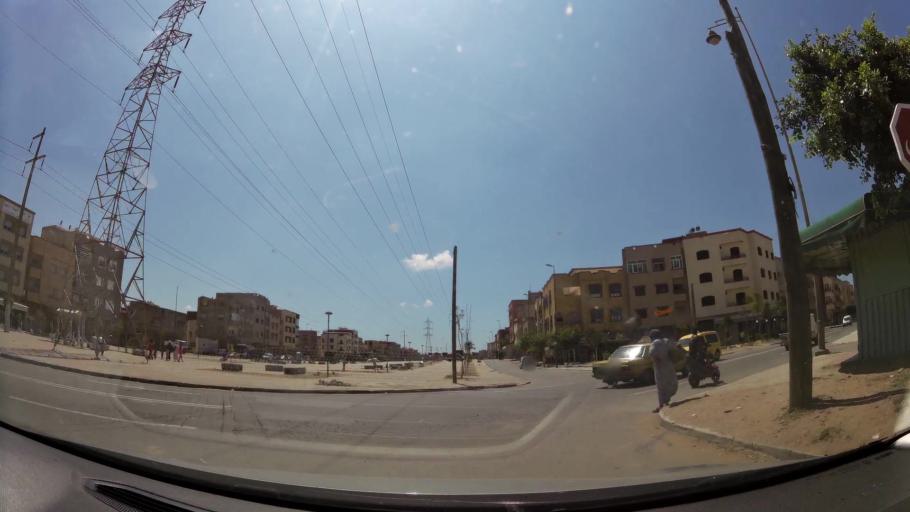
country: MA
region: Gharb-Chrarda-Beni Hssen
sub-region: Kenitra Province
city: Kenitra
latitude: 34.2377
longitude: -6.5452
